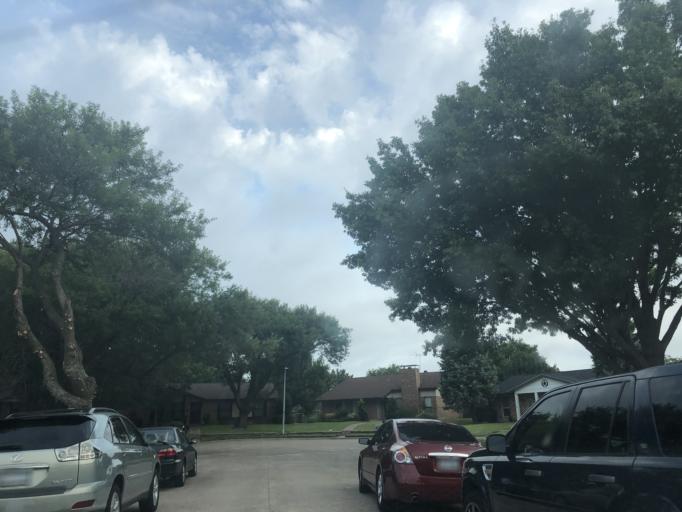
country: US
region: Texas
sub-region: Dallas County
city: Garland
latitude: 32.8456
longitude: -96.6248
